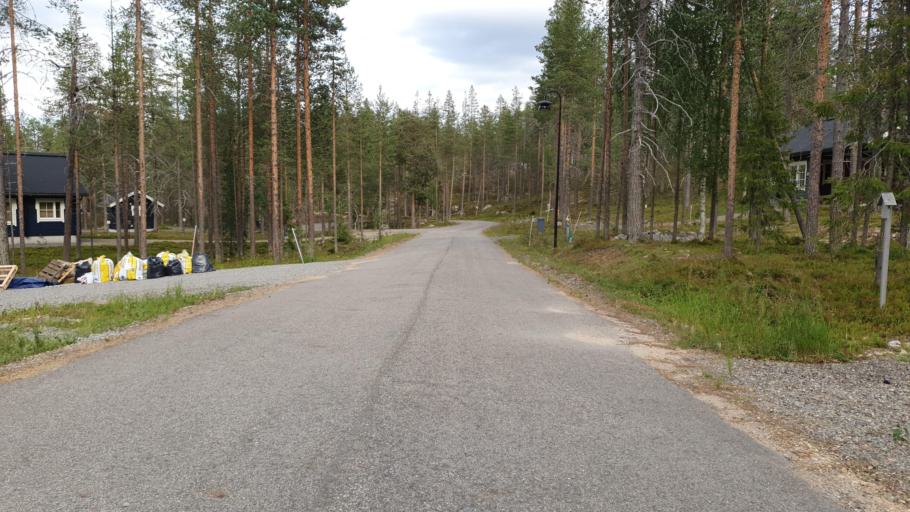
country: FI
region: Lapland
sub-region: Tunturi-Lappi
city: Kolari
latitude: 67.5913
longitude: 24.1285
